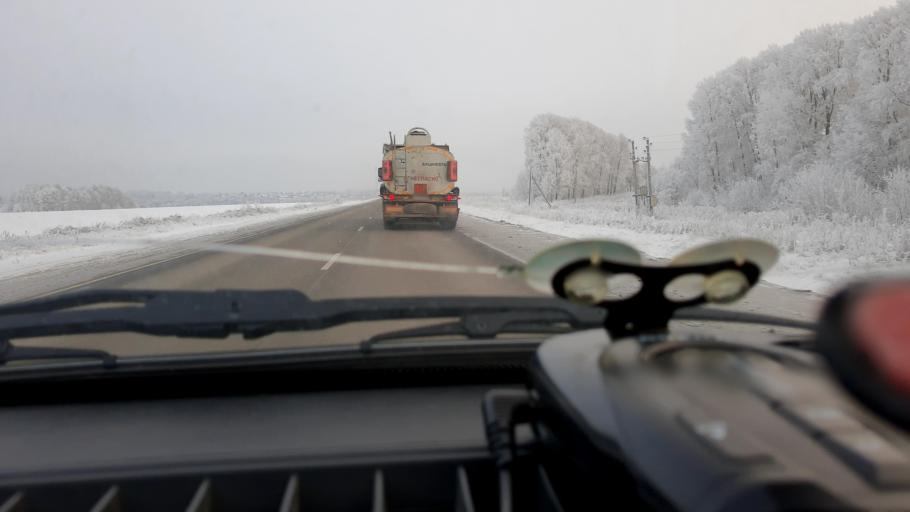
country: RU
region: Bashkortostan
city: Blagoveshchensk
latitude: 55.0692
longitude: 55.9118
